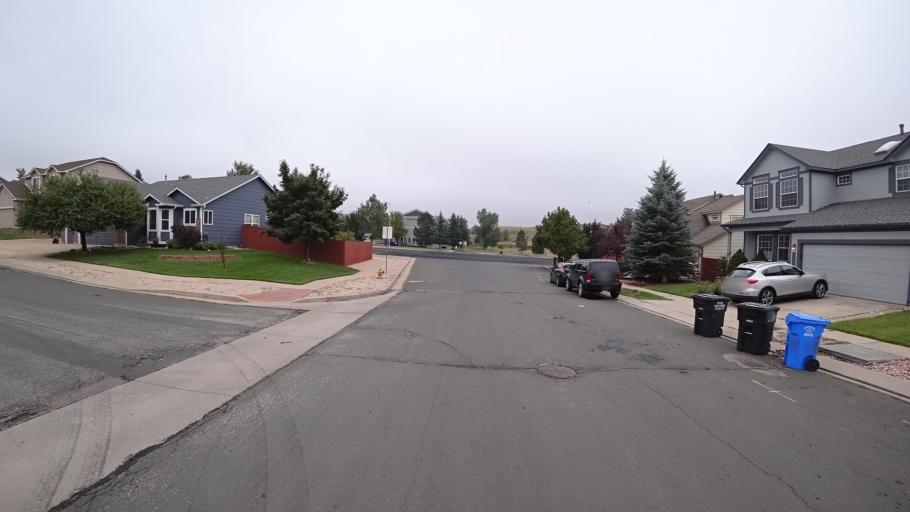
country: US
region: Colorado
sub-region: El Paso County
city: Cimarron Hills
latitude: 38.9301
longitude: -104.7491
